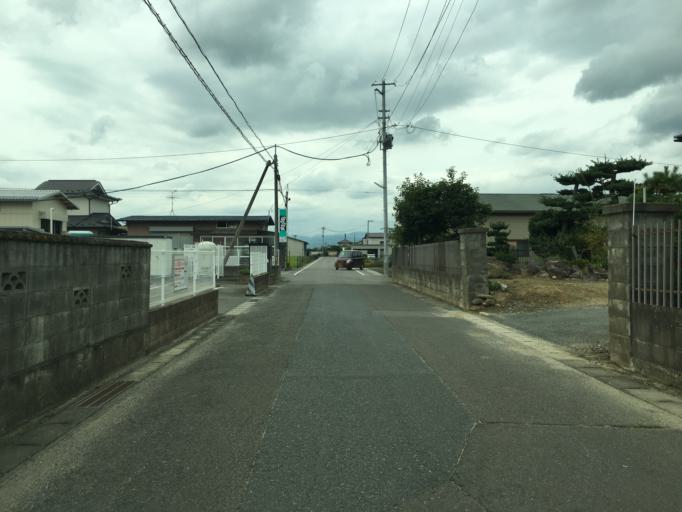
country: JP
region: Fukushima
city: Hobaramachi
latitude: 37.8177
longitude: 140.5457
